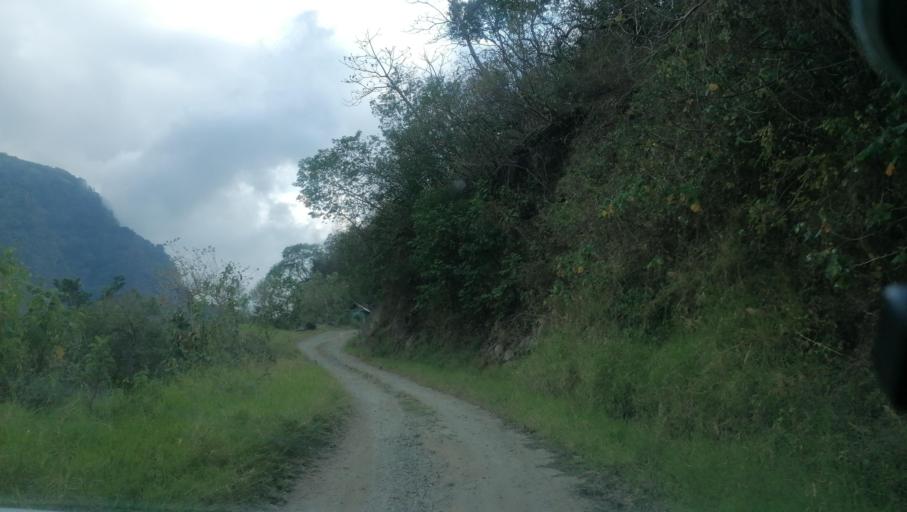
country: MX
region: Chiapas
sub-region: Cacahoatan
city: Benito Juarez
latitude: 15.1429
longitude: -92.1895
